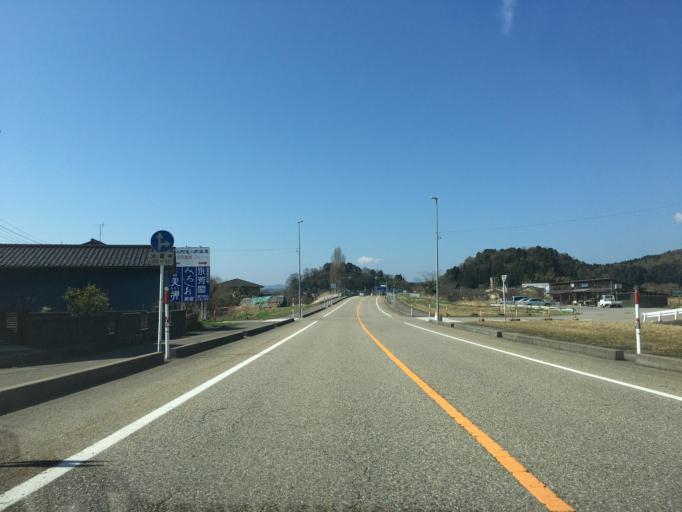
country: JP
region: Toyama
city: Himi
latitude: 36.8859
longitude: 136.9951
